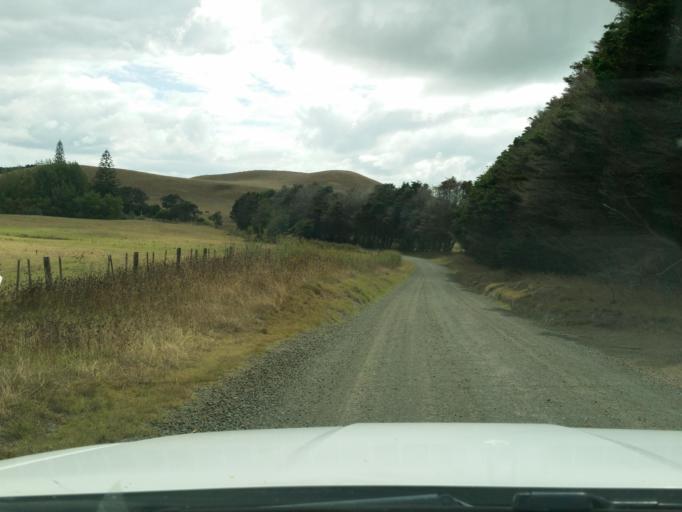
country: NZ
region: Auckland
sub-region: Auckland
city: Wellsford
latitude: -36.3440
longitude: 174.1682
